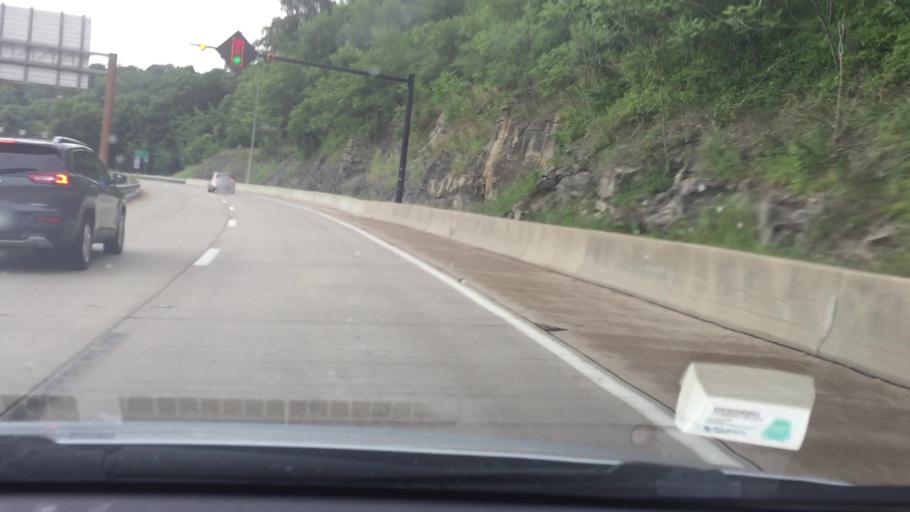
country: US
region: Pennsylvania
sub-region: Allegheny County
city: Etna
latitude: 40.5011
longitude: -79.9424
